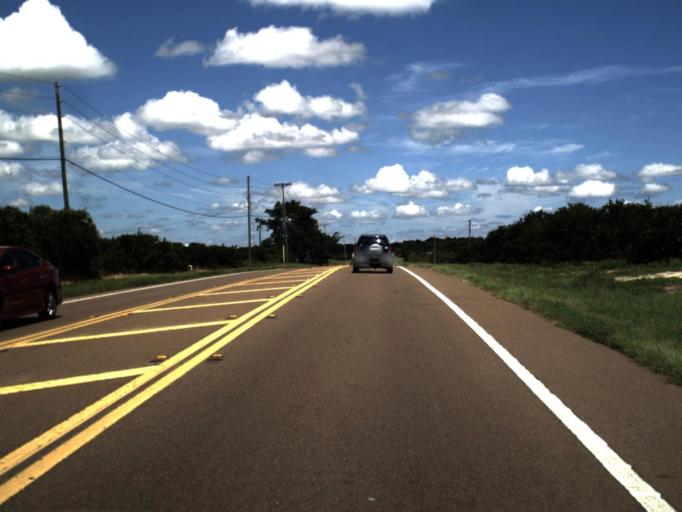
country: US
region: Florida
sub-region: Polk County
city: Lake Wales
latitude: 27.8739
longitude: -81.5813
